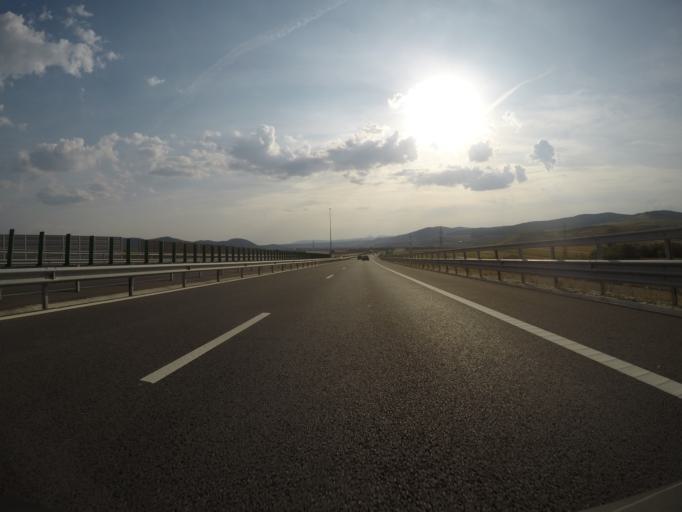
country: RO
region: Alba
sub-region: Comuna Unirea
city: Unirea
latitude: 46.3914
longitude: 23.7827
